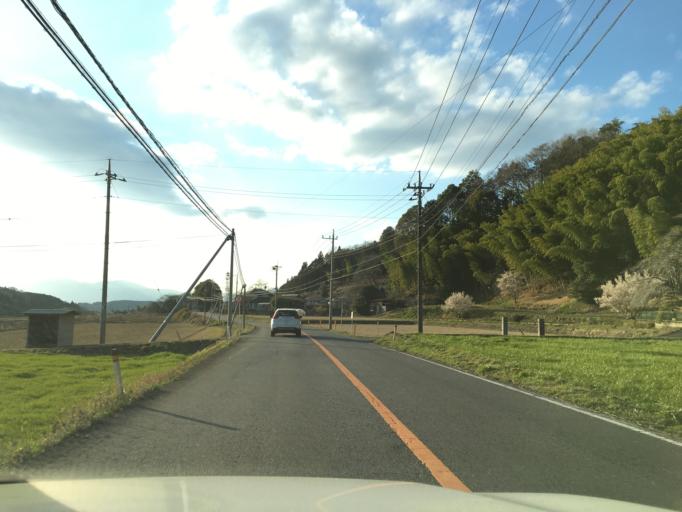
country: JP
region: Tochigi
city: Otawara
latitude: 36.8668
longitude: 140.1589
